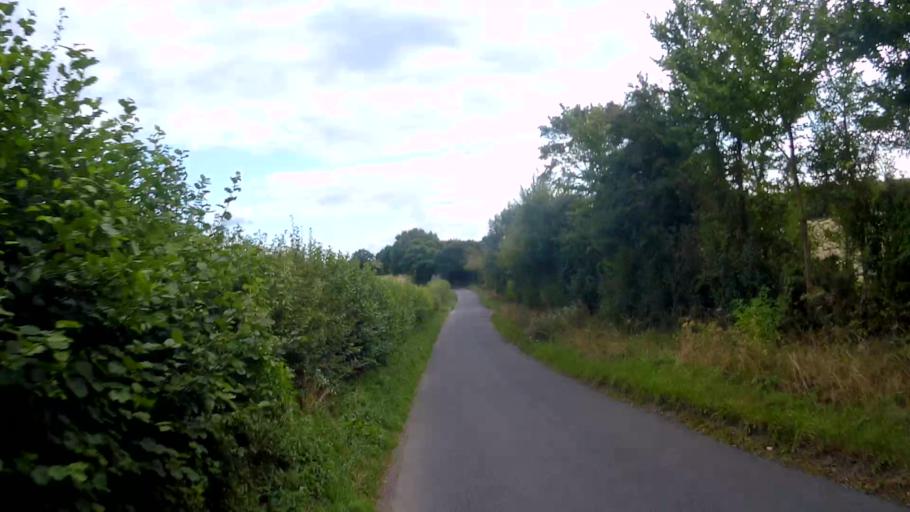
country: GB
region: England
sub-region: Hampshire
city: Kings Worthy
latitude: 51.1508
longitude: -1.2219
